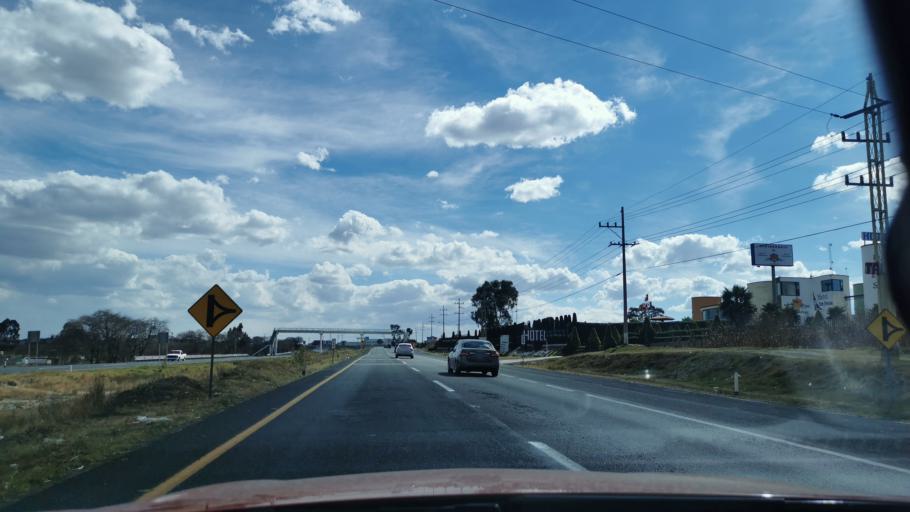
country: MX
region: Mexico
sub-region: Jocotitlan
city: Santa Maria Endare
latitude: 19.7323
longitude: -99.8427
